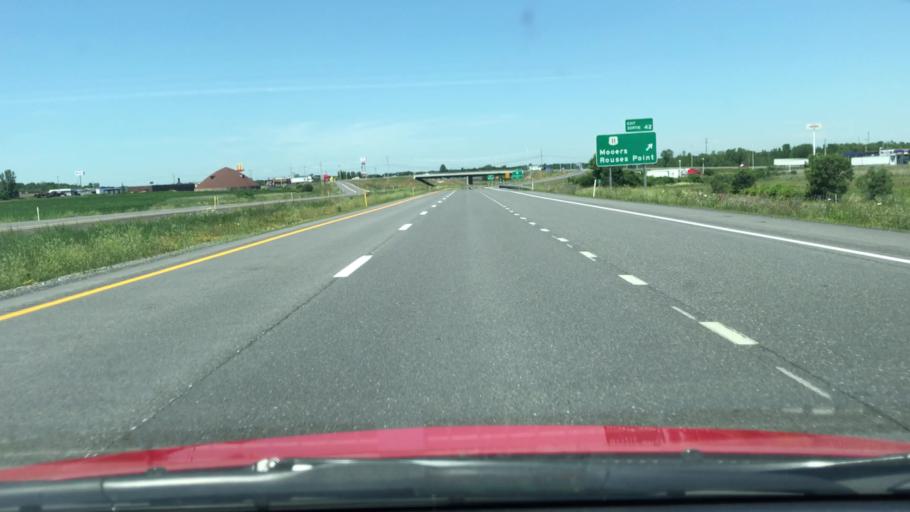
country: US
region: New York
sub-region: Clinton County
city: Champlain
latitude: 44.9767
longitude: -73.4549
